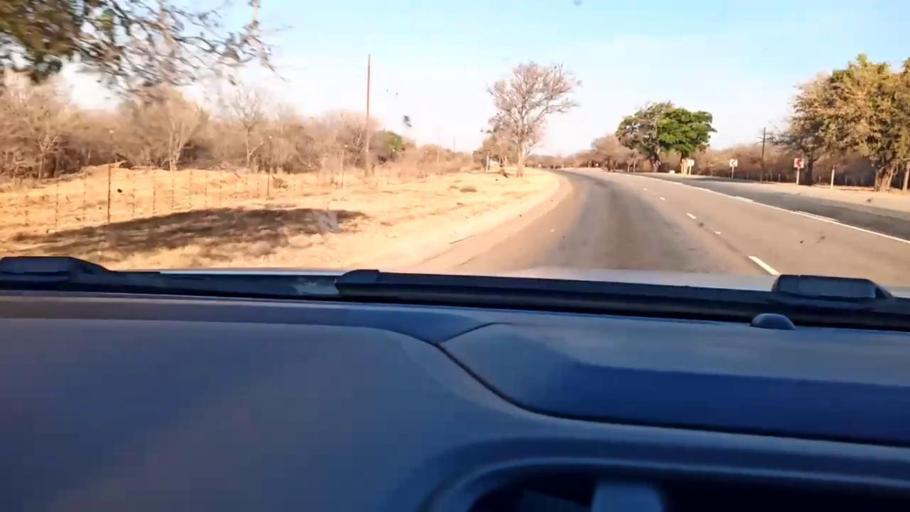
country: ZA
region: Limpopo
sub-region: Mopani District Municipality
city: Duiwelskloof
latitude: -23.6167
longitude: 30.1188
